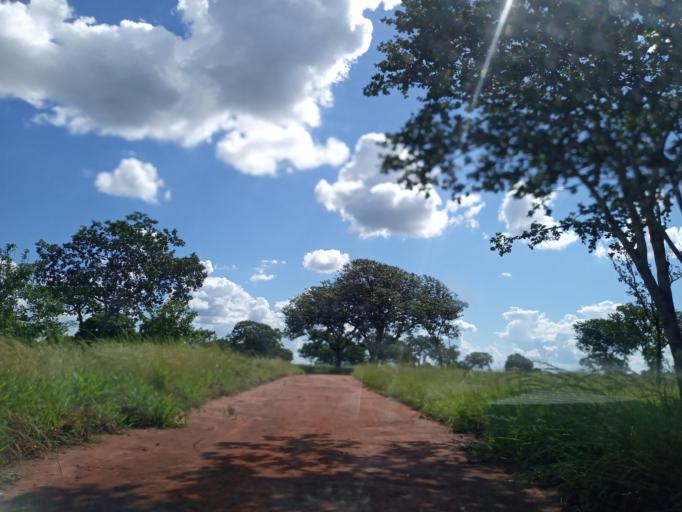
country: BR
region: Minas Gerais
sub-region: Ituiutaba
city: Ituiutaba
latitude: -18.9691
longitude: -49.4999
